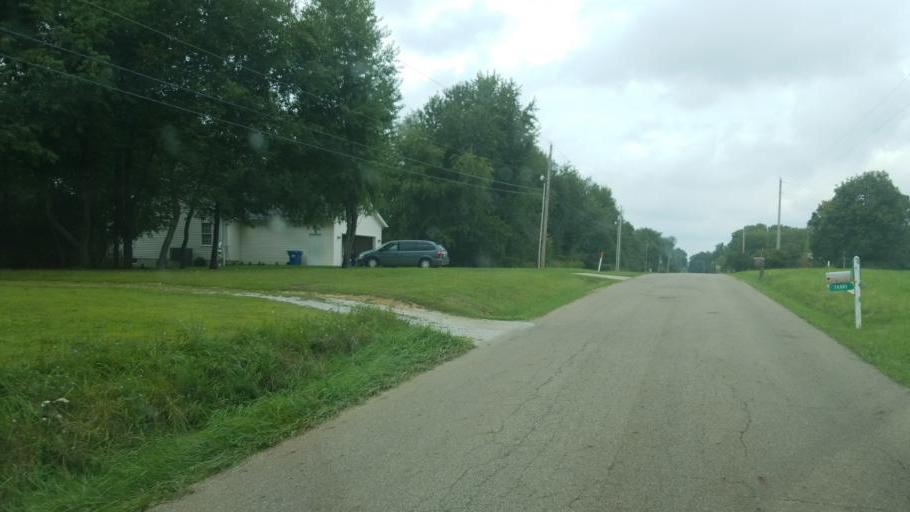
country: US
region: Ohio
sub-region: Knox County
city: Danville
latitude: 40.4478
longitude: -82.3277
